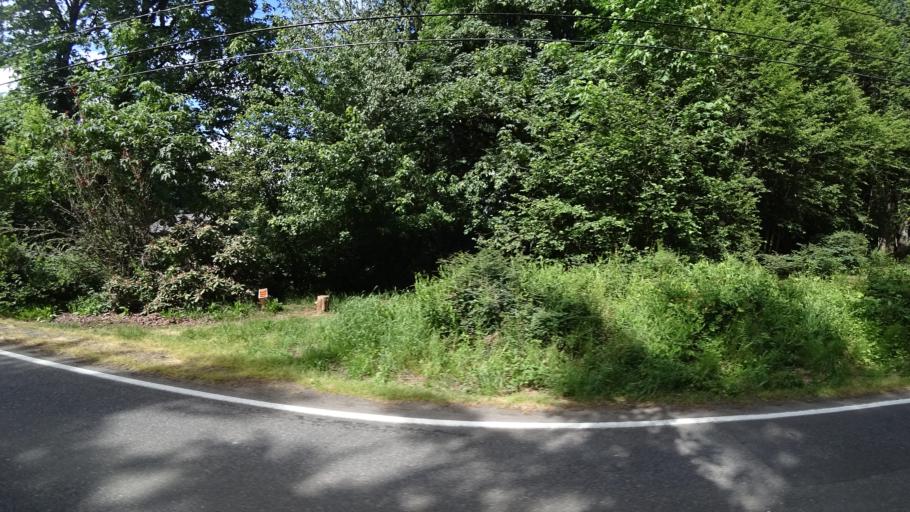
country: US
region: Oregon
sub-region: Washington County
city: Oak Hills
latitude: 45.5886
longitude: -122.8073
